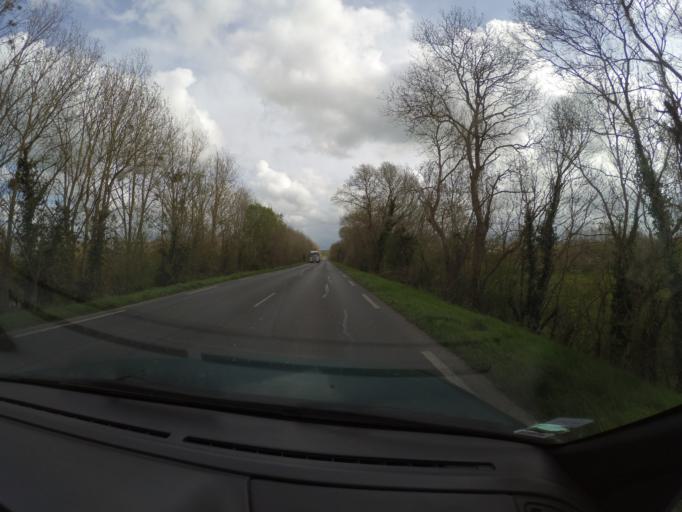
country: FR
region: Pays de la Loire
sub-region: Departement de Maine-et-Loire
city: Lire
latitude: 47.3537
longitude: -1.1708
